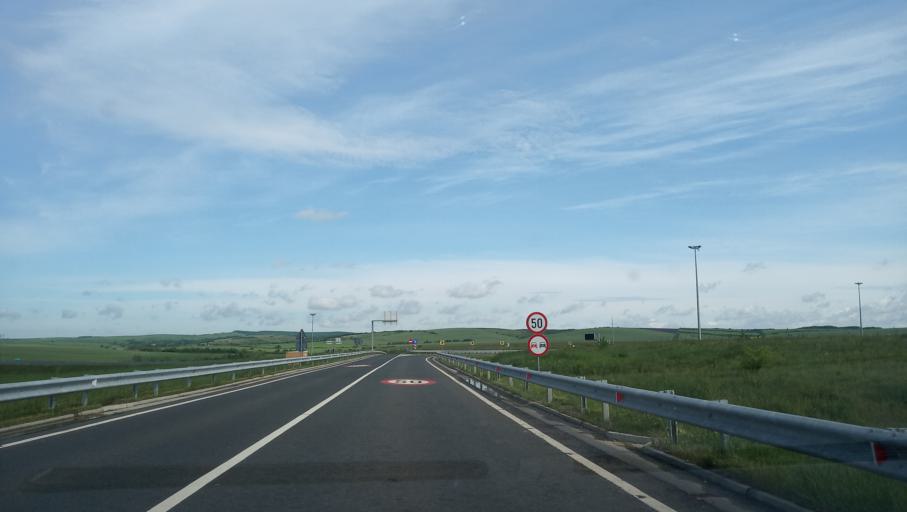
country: RO
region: Timis
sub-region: Comuna Topolovatu Mare
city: Topolovatu Mare
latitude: 45.7985
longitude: 21.6581
